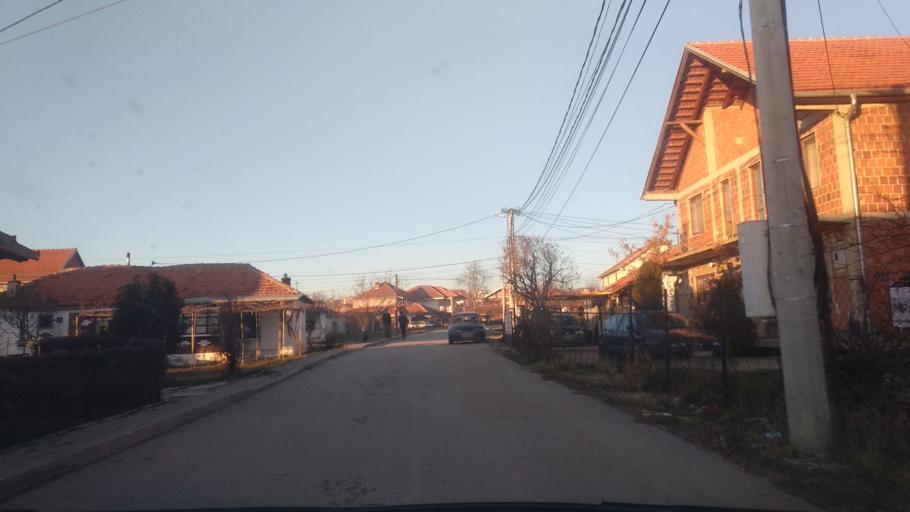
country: XK
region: Pristina
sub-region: Komuna e Prishtines
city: Pristina
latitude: 42.6046
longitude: 21.1828
